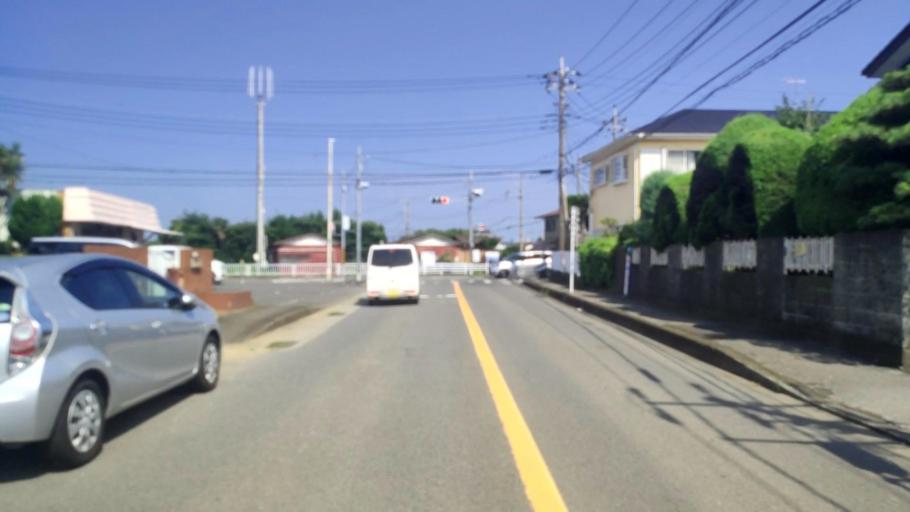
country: JP
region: Kanagawa
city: Isehara
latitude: 35.3688
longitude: 139.3152
